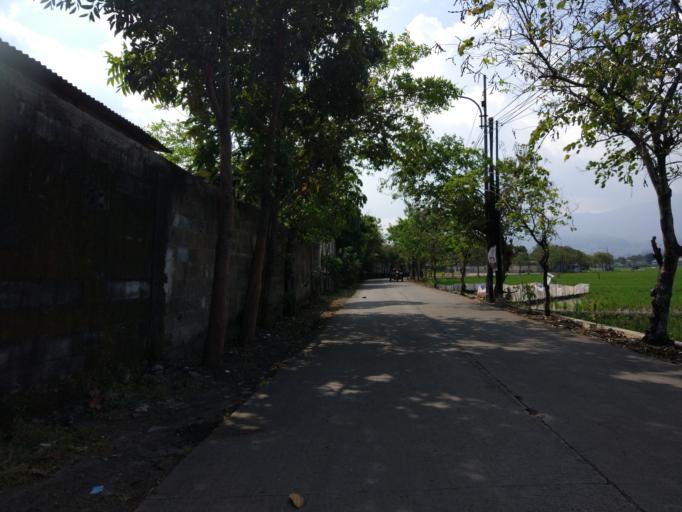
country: ID
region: West Java
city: Cileunyi
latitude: -6.9352
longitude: 107.7064
